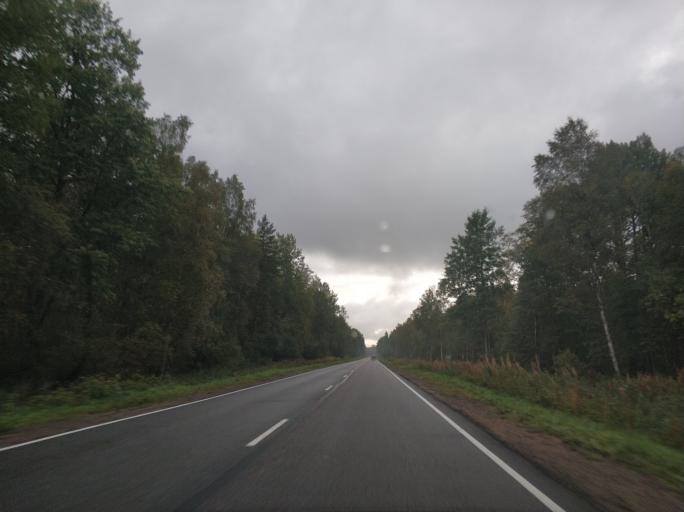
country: RU
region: Leningrad
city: Borisova Griva
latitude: 60.1237
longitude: 30.9634
